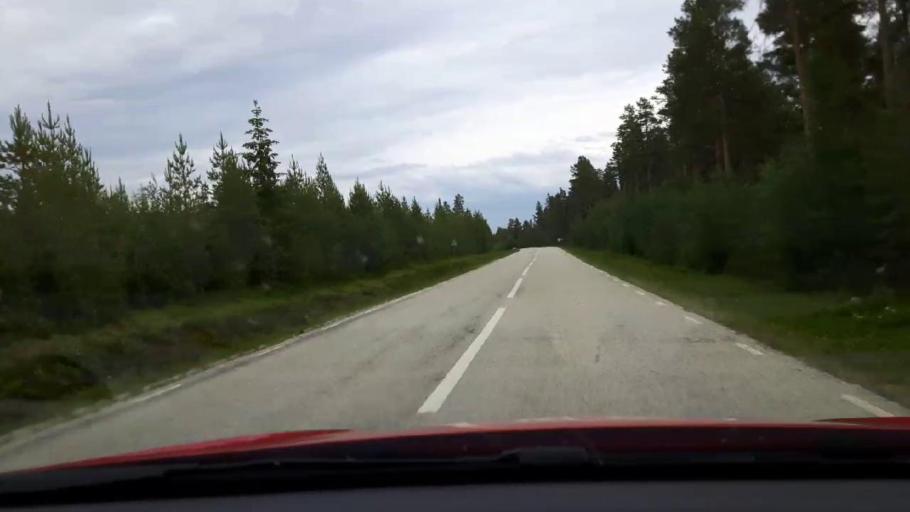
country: SE
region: Jaemtland
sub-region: Bergs Kommun
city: Hoverberg
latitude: 62.7195
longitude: 13.9151
